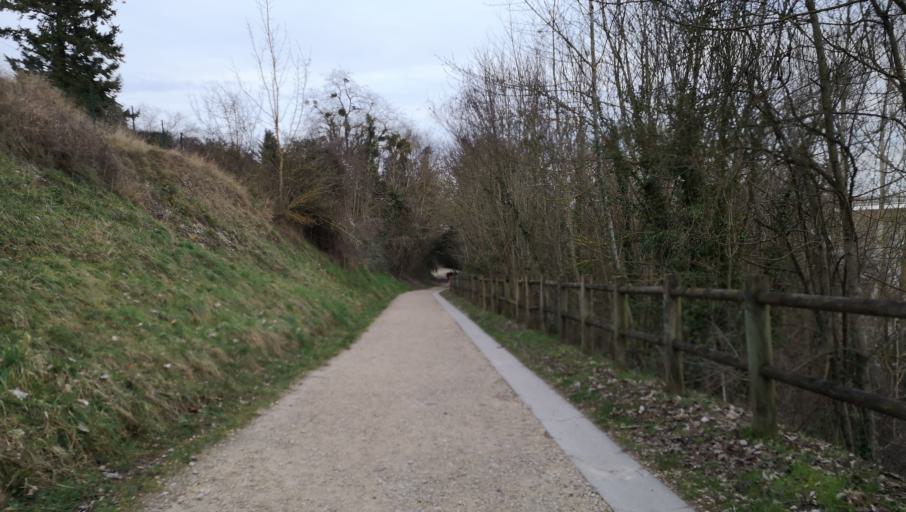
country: FR
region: Centre
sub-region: Departement du Loiret
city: La Chapelle-Saint-Mesmin
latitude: 47.8925
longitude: 1.8530
